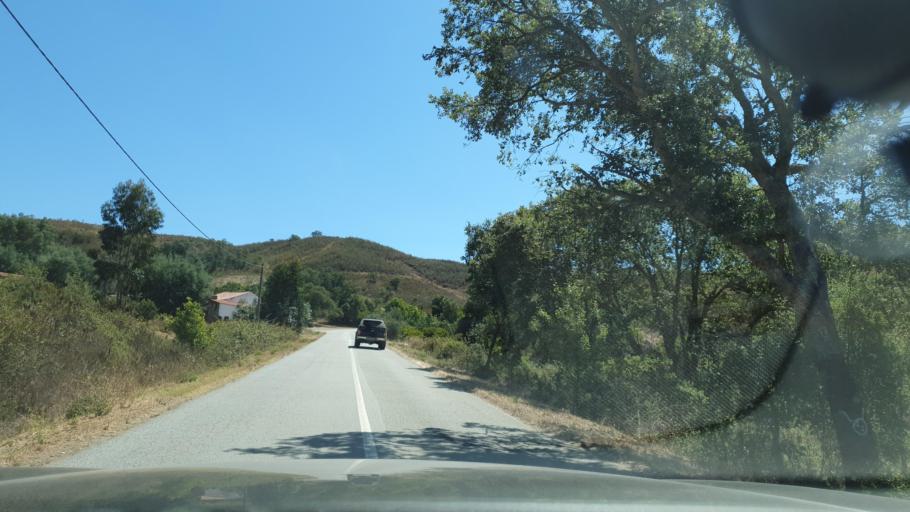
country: PT
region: Faro
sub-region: Monchique
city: Monchique
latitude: 37.4208
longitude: -8.5493
